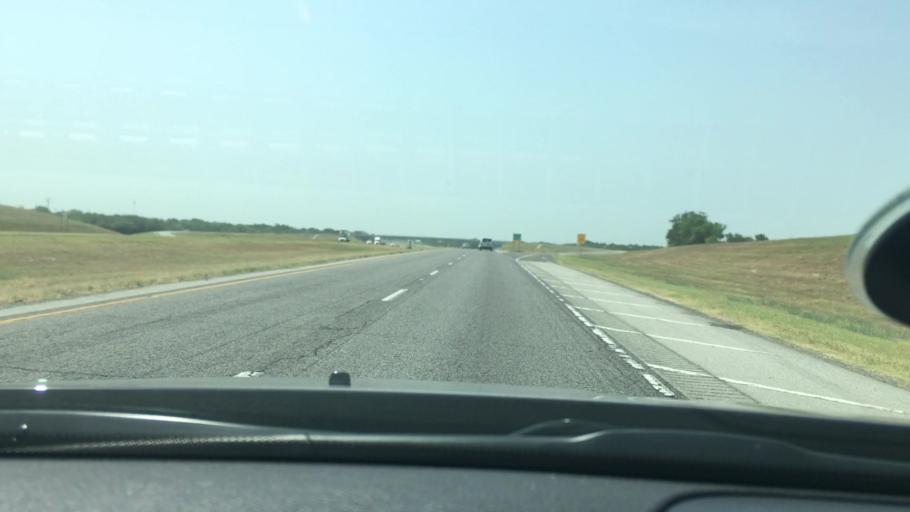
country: US
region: Oklahoma
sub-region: Garvin County
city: Wynnewood
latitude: 34.5767
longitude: -97.2011
